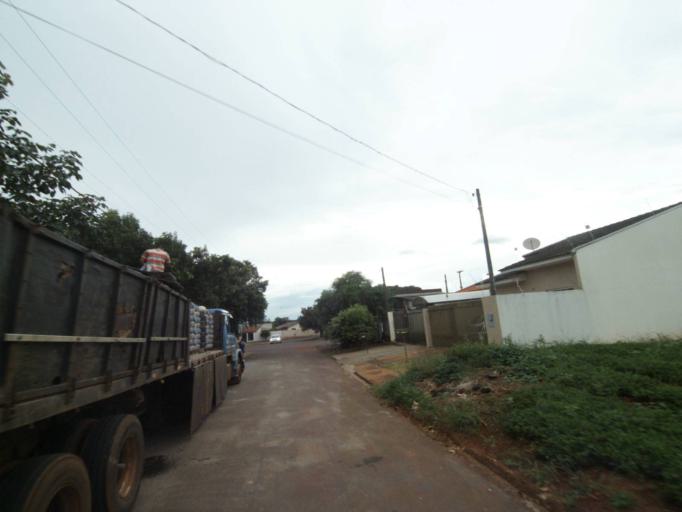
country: BR
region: Parana
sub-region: Campo Mourao
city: Campo Mourao
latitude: -24.0260
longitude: -52.3573
